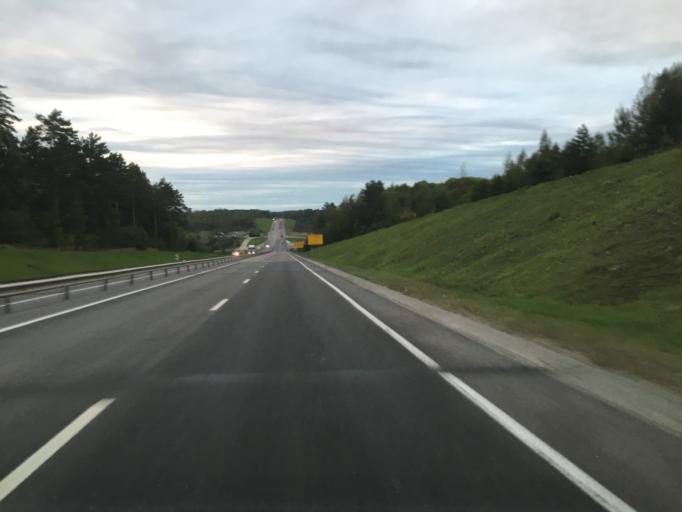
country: RU
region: Kaluga
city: Kaluga
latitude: 54.5955
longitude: 36.3247
